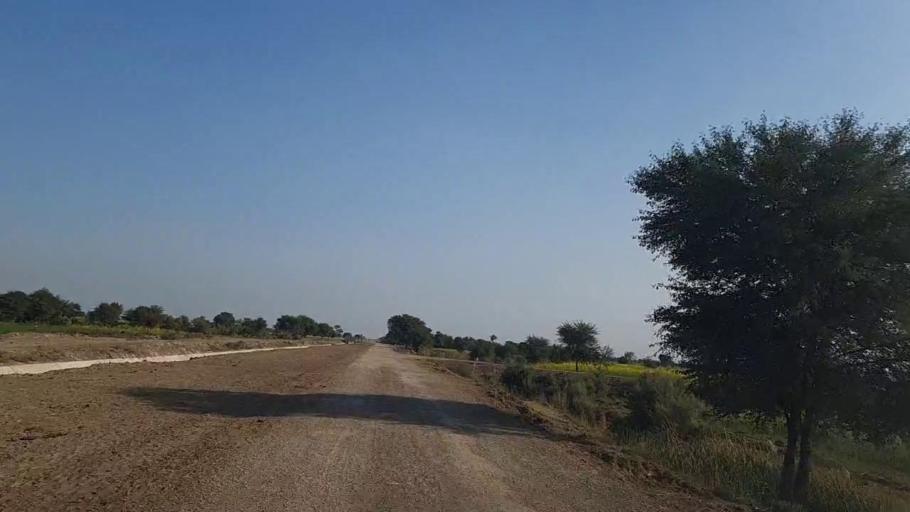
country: PK
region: Sindh
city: Shahpur Chakar
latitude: 26.2000
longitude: 68.6497
